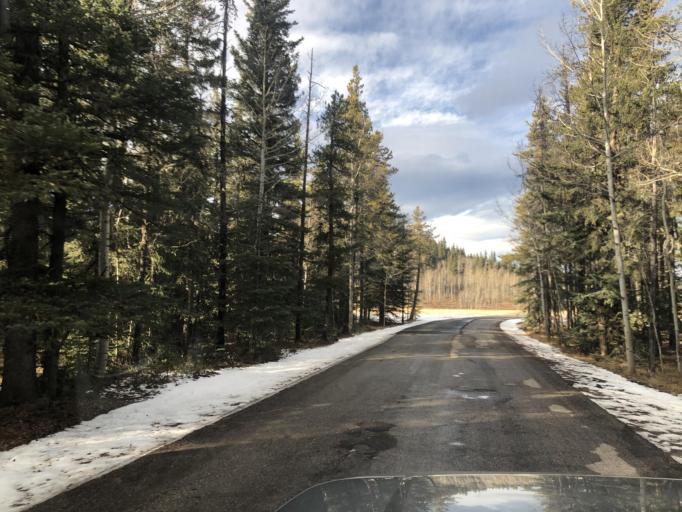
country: CA
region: Alberta
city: Cochrane
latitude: 51.0428
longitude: -114.8662
